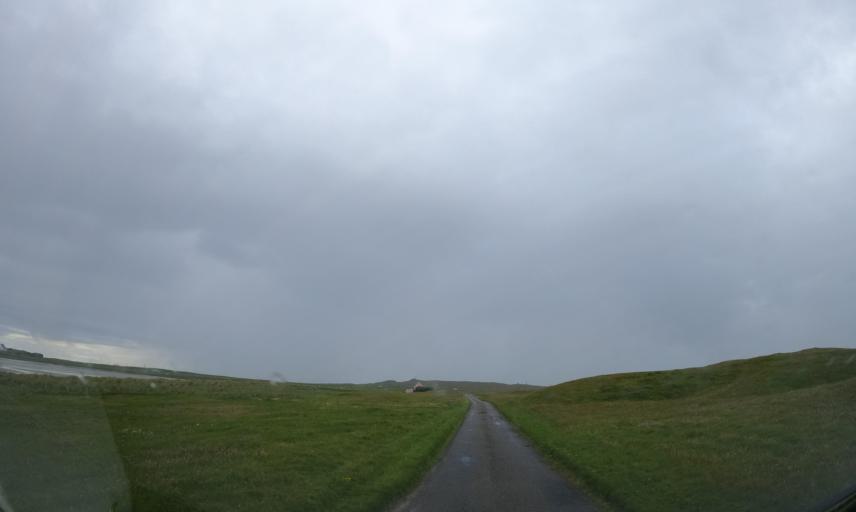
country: GB
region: Scotland
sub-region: Eilean Siar
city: Barra
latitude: 56.5160
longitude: -6.8146
